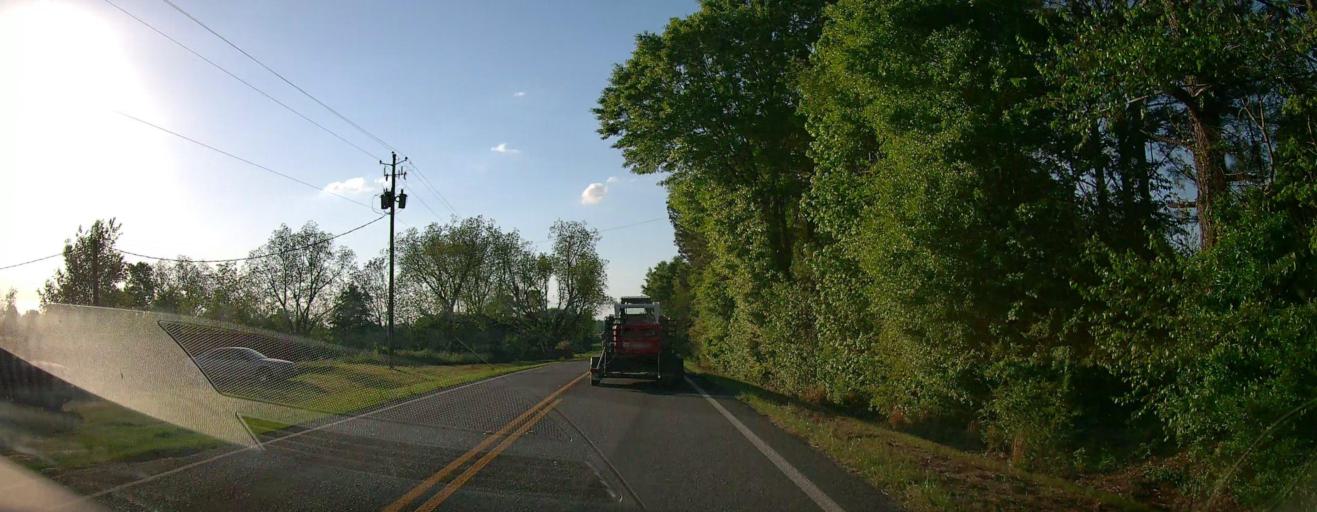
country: US
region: Georgia
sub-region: Jasper County
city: Monticello
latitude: 33.4429
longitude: -83.6226
